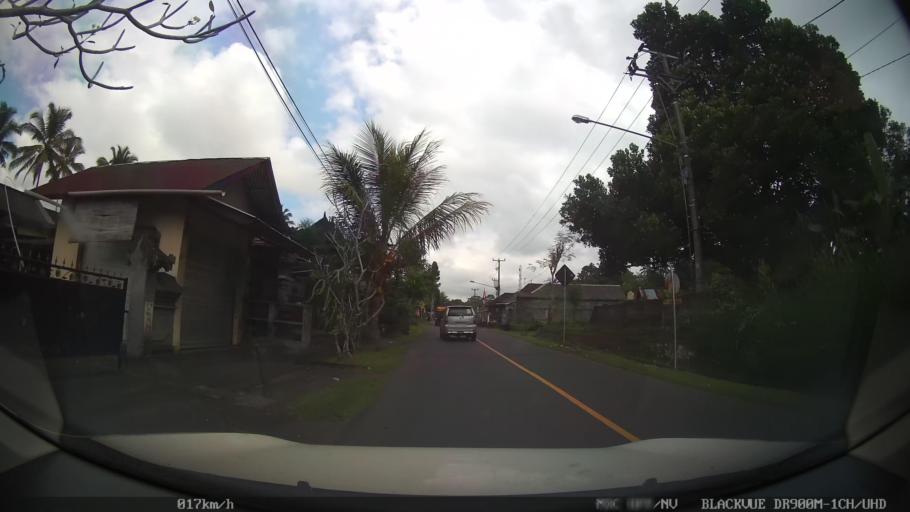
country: ID
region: Bali
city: Banjar Kubu
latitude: -8.4104
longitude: 115.4252
